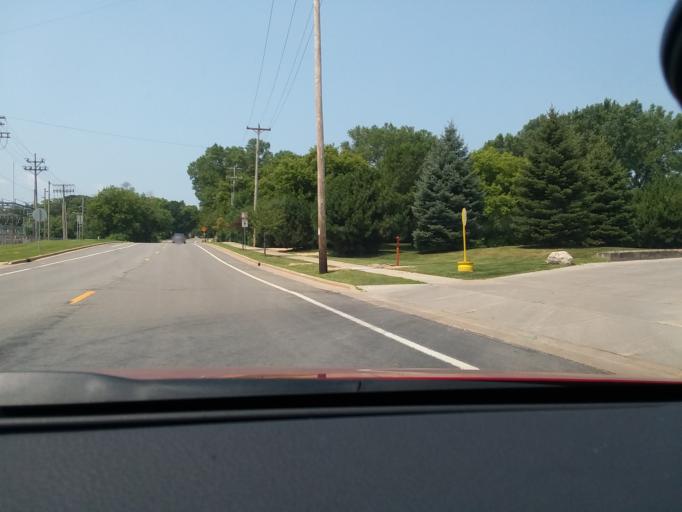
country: US
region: Wisconsin
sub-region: Dane County
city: Monona
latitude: 43.1138
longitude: -89.3118
